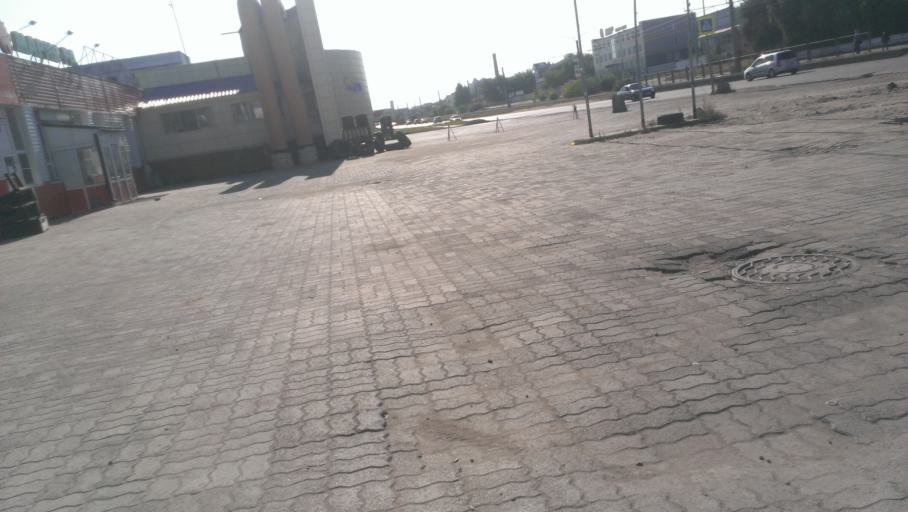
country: RU
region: Altai Krai
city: Novosilikatnyy
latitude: 53.3232
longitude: 83.6429
